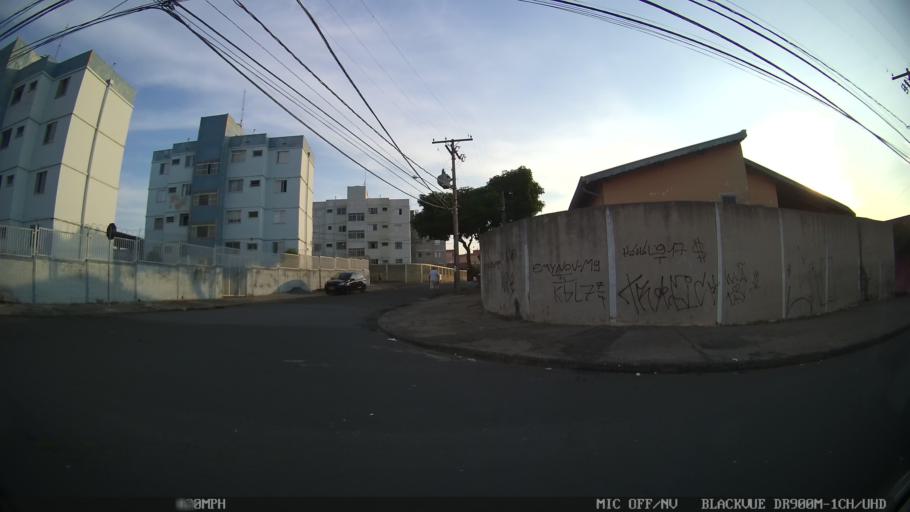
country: BR
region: Sao Paulo
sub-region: Campinas
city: Campinas
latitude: -22.9790
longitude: -47.1300
